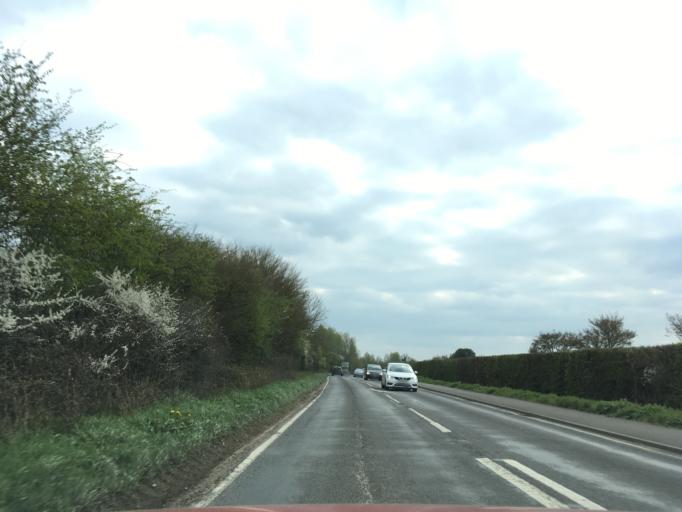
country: GB
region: England
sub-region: Oxfordshire
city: North Leigh
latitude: 51.8006
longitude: -1.4583
